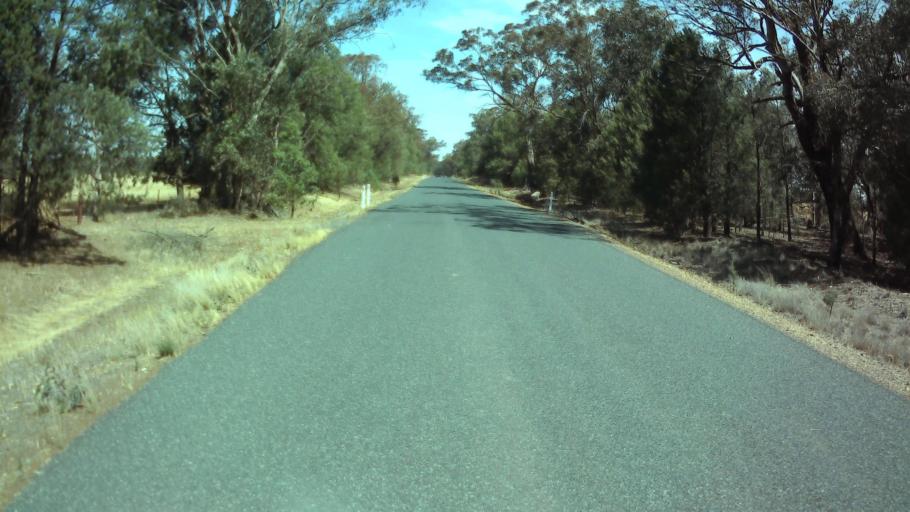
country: AU
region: New South Wales
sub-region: Weddin
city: Grenfell
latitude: -34.0624
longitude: 148.1341
